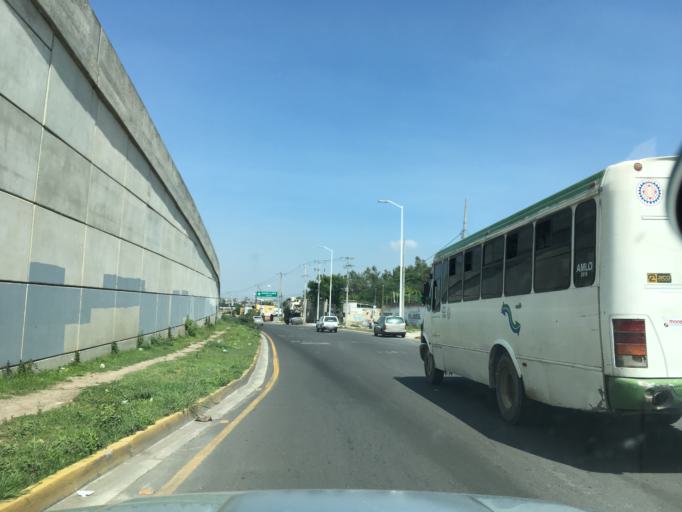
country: MX
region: Jalisco
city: Tonala
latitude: 20.6846
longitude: -103.2462
